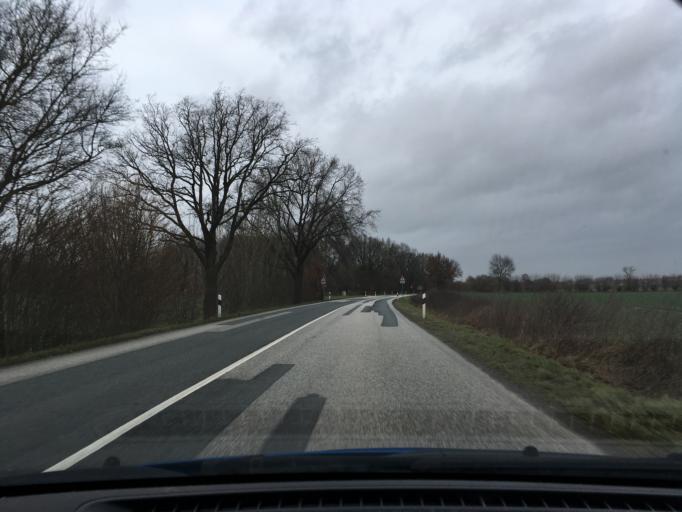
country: DE
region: Schleswig-Holstein
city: Kruzen
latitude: 53.4133
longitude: 10.5363
